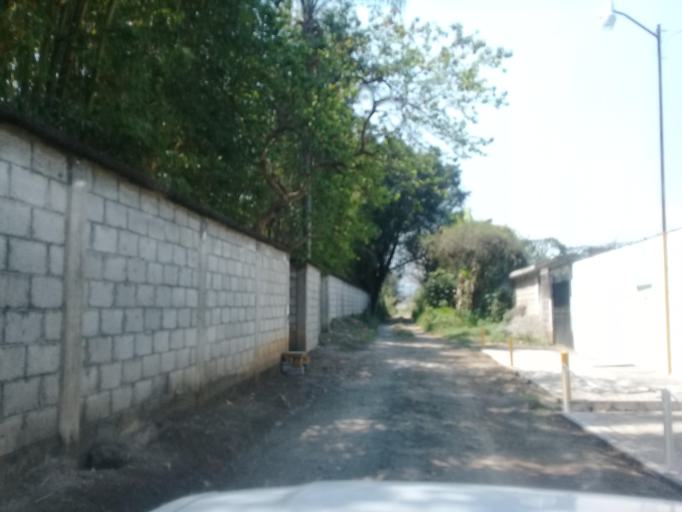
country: MX
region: Veracruz
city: Ixtac Zoquitlan
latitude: 18.8742
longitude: -97.0496
